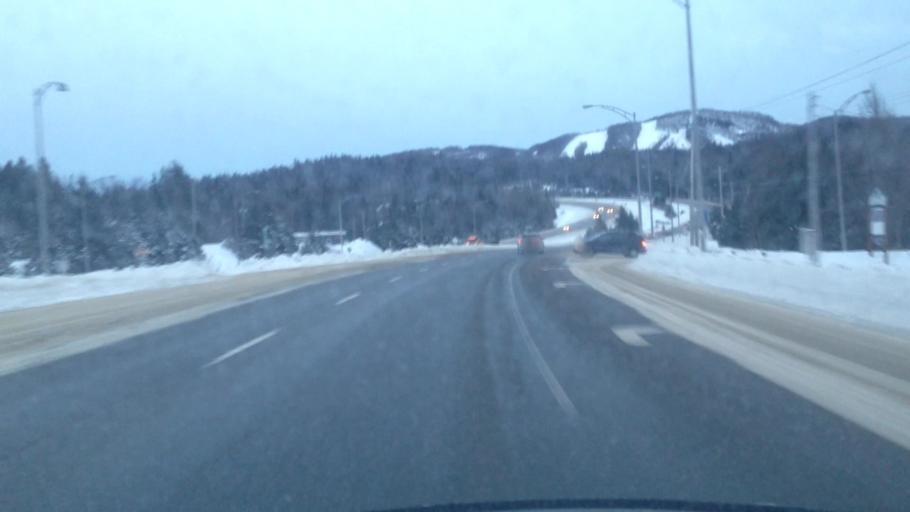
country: CA
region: Quebec
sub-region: Laurentides
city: Mont-Tremblant
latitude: 46.1124
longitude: -74.5191
